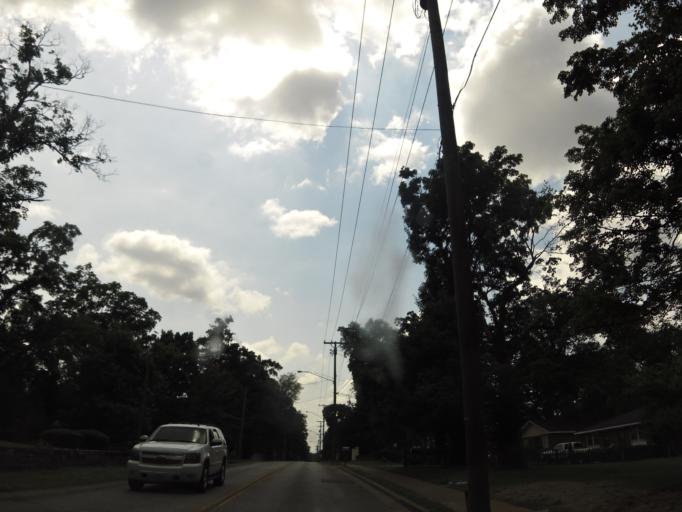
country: US
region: Tennessee
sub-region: Davidson County
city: Oak Hill
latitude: 36.1206
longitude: -86.7810
